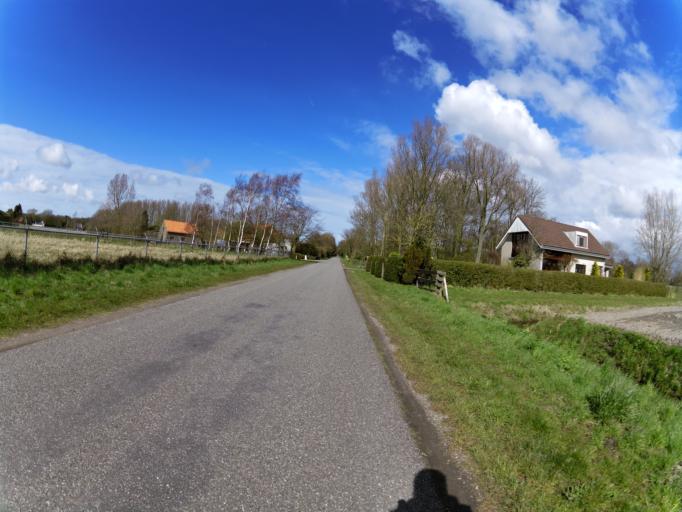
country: NL
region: South Holland
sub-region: Gemeente Hellevoetsluis
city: Nieuw-Helvoet
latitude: 51.8880
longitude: 4.0741
